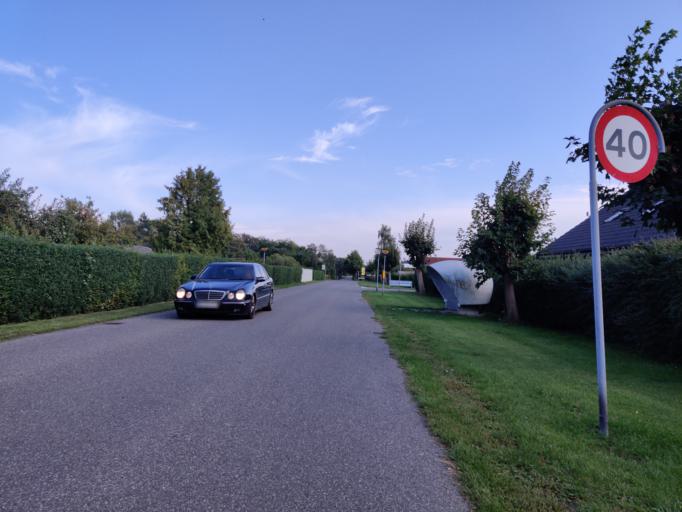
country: DK
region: Zealand
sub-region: Guldborgsund Kommune
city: Nykobing Falster
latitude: 54.7076
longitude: 11.9282
